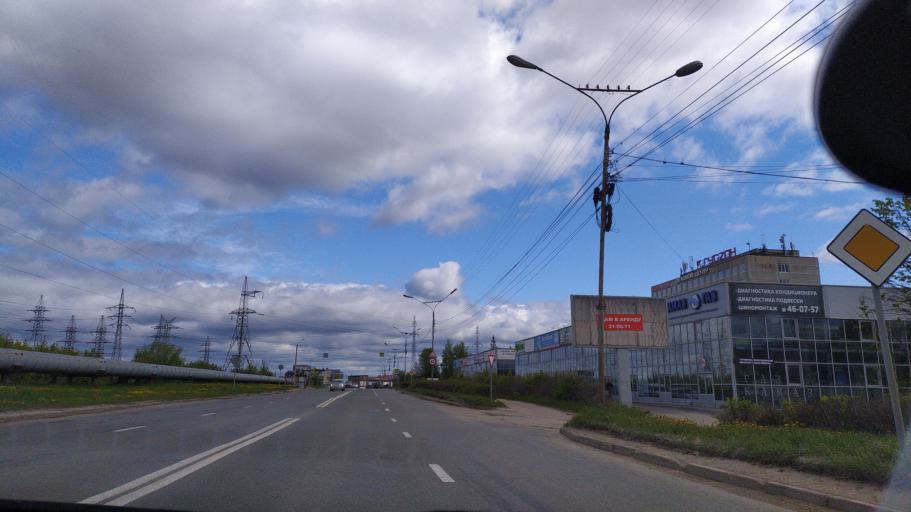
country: RU
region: Chuvashia
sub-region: Cheboksarskiy Rayon
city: Cheboksary
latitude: 56.1247
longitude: 47.3071
